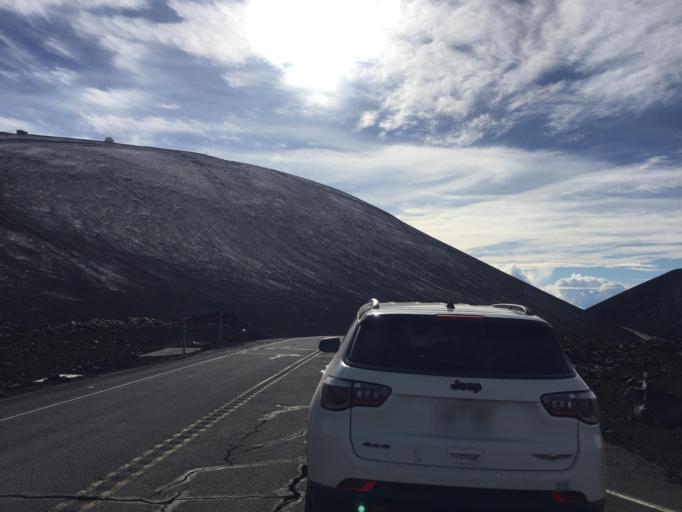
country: US
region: Hawaii
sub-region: Hawaii County
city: Honoka'a
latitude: 19.8227
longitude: -155.4754
